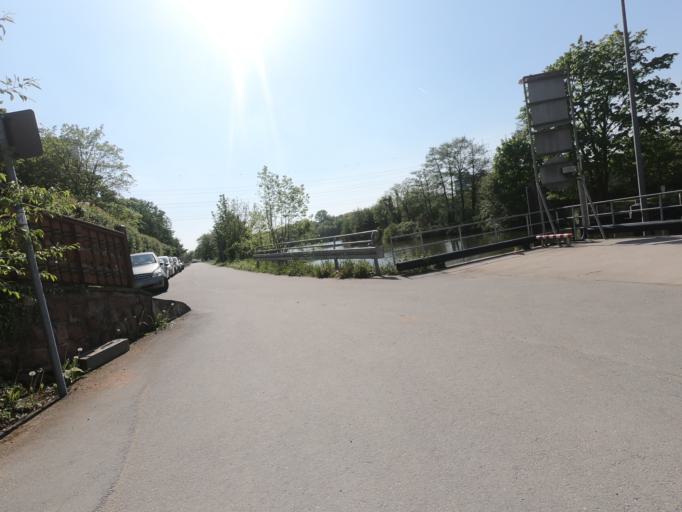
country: DE
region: Hesse
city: Kelsterbach
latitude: 50.0560
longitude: 8.5133
